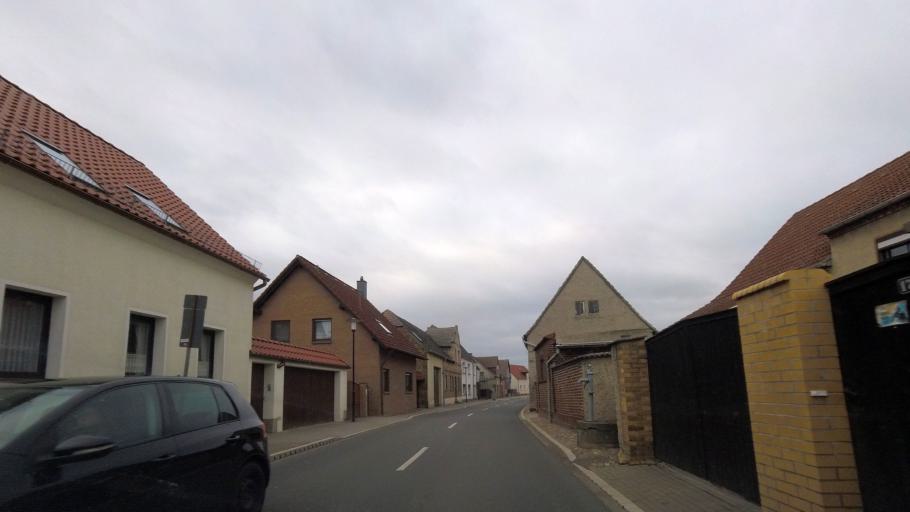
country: DE
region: Saxony-Anhalt
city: Kemberg
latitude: 51.7729
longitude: 12.6336
